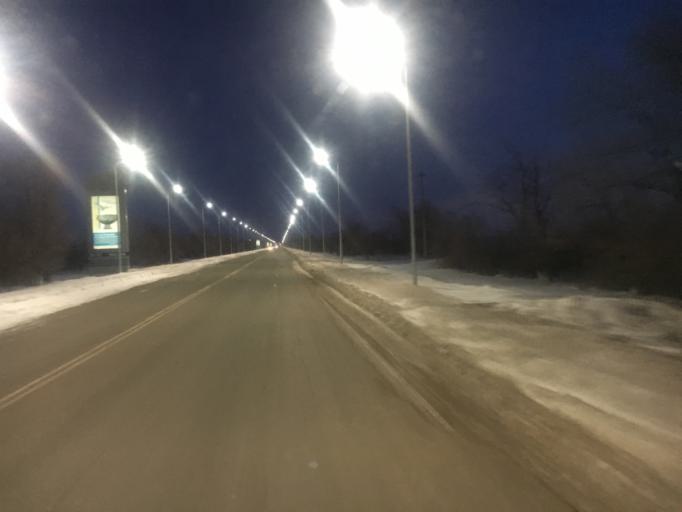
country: KZ
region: Batys Qazaqstan
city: Oral
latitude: 51.1639
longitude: 51.5257
